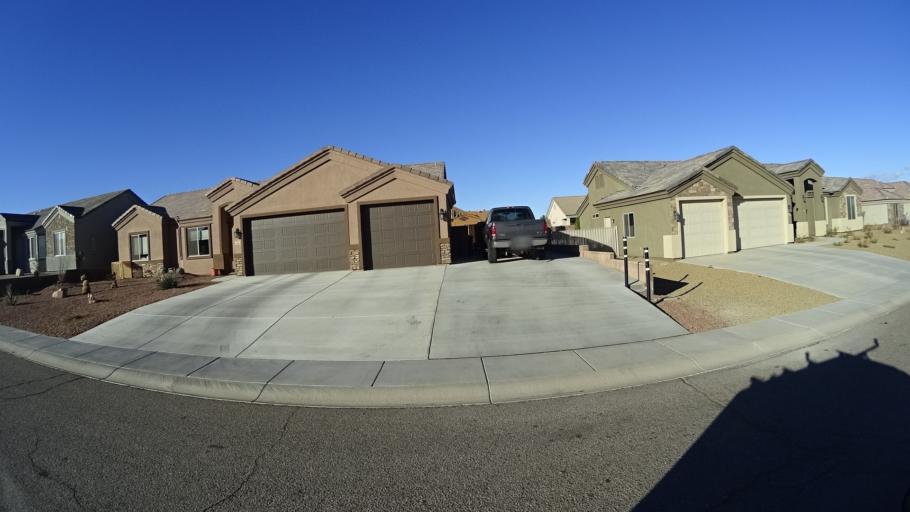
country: US
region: Arizona
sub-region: Mohave County
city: New Kingman-Butler
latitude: 35.2195
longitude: -113.9699
